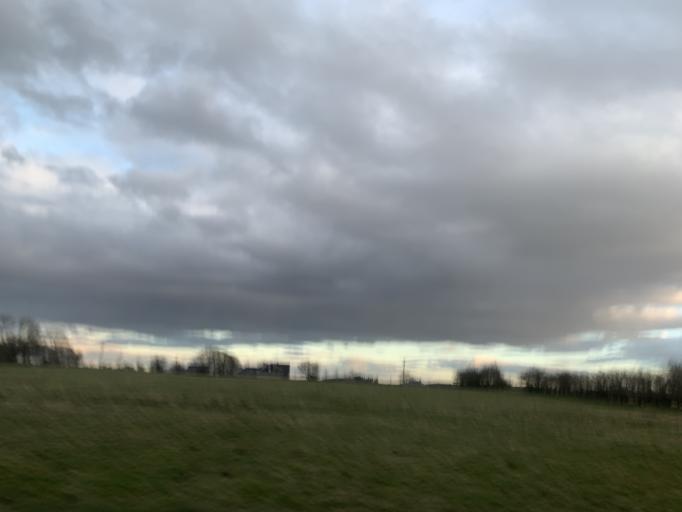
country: IE
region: Connaught
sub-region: Sligo
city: Tobercurry
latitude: 54.0684
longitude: -8.7085
